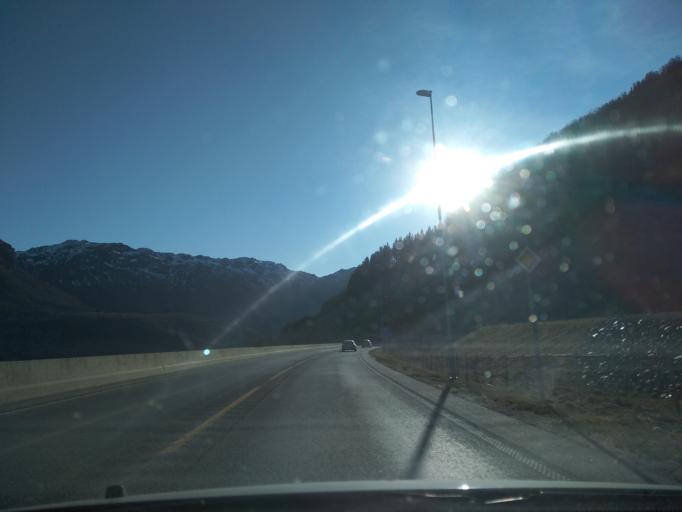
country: NO
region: Hordaland
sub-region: Etne
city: Etne
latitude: 59.7241
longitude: 6.1188
